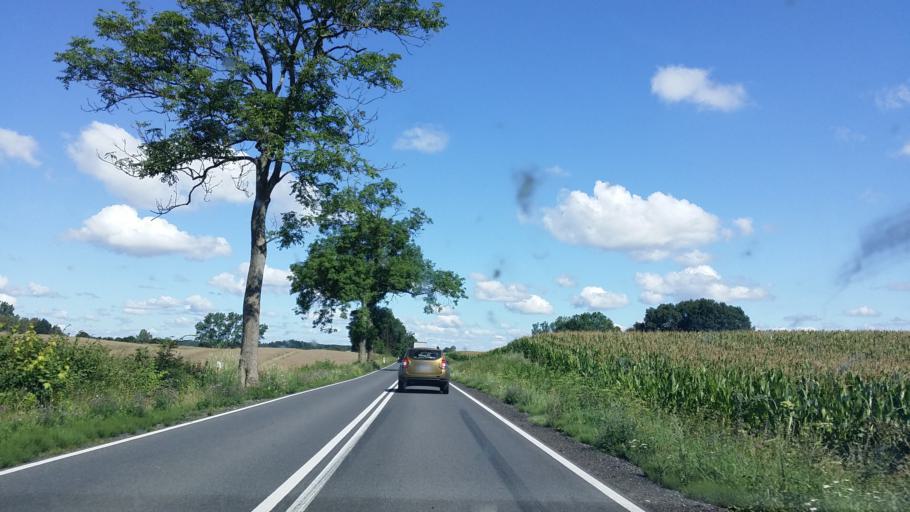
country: PL
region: West Pomeranian Voivodeship
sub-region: Powiat drawski
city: Kalisz Pomorski
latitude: 53.3208
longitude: 15.9035
